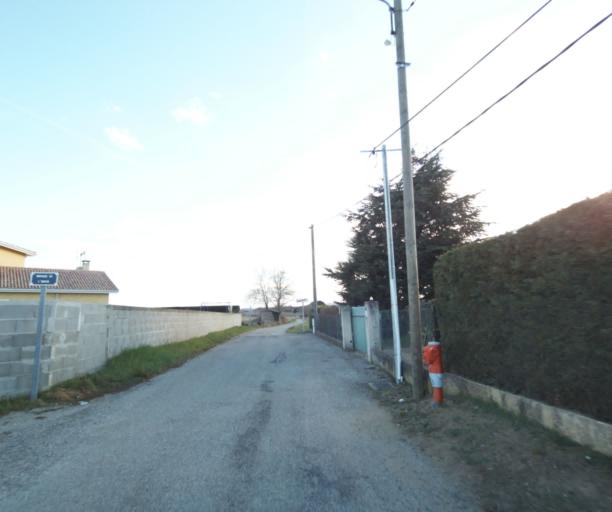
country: FR
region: Rhone-Alpes
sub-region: Departement de l'Ardeche
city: Davezieux
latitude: 45.2465
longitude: 4.7055
